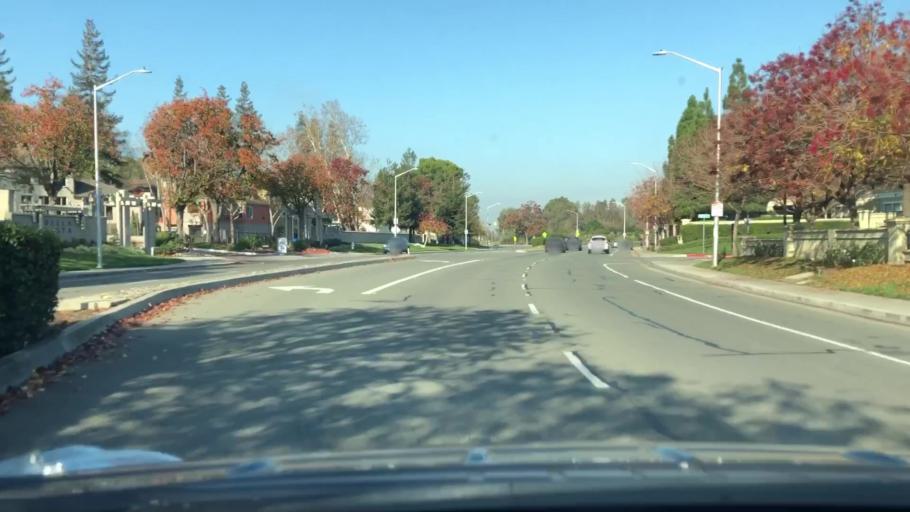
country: US
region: California
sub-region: Santa Clara County
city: Santa Clara
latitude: 37.4023
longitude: -121.9532
